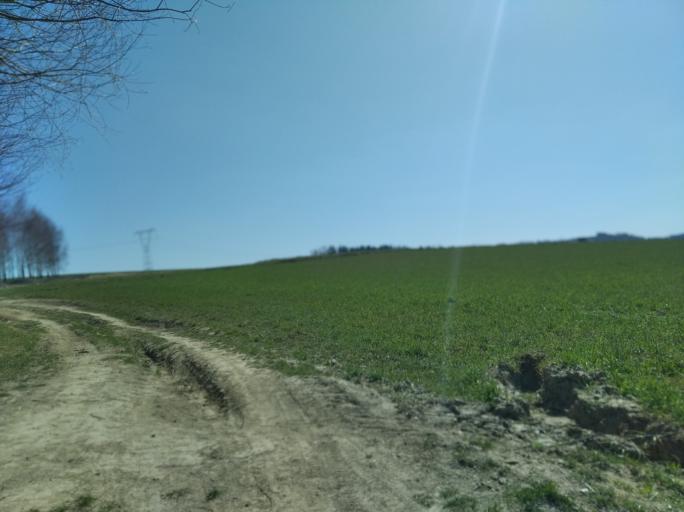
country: PL
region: Subcarpathian Voivodeship
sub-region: Powiat strzyzowski
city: Polomia
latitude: 49.8833
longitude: 21.8465
